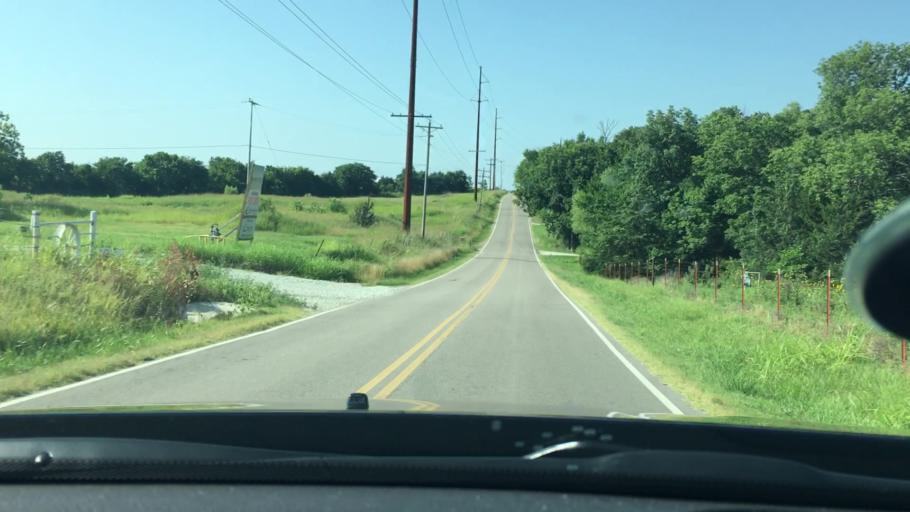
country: US
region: Oklahoma
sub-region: Pontotoc County
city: Ada
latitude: 34.7995
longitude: -96.6348
